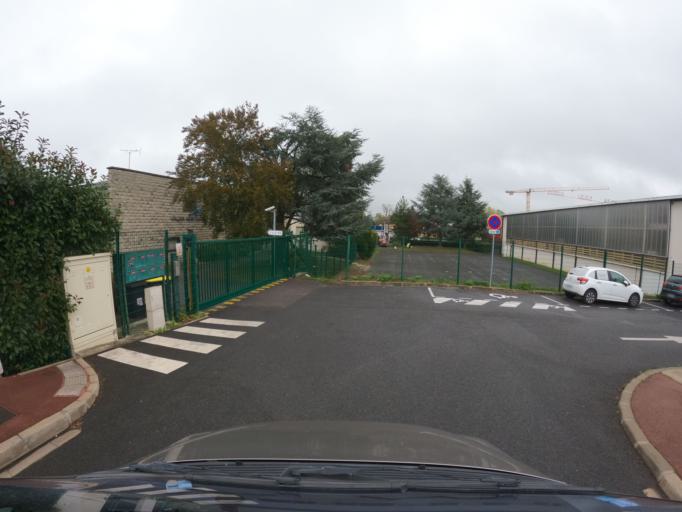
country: FR
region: Ile-de-France
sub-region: Departement du Val-de-Marne
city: Ormesson-sur-Marne
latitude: 48.7924
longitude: 2.5522
